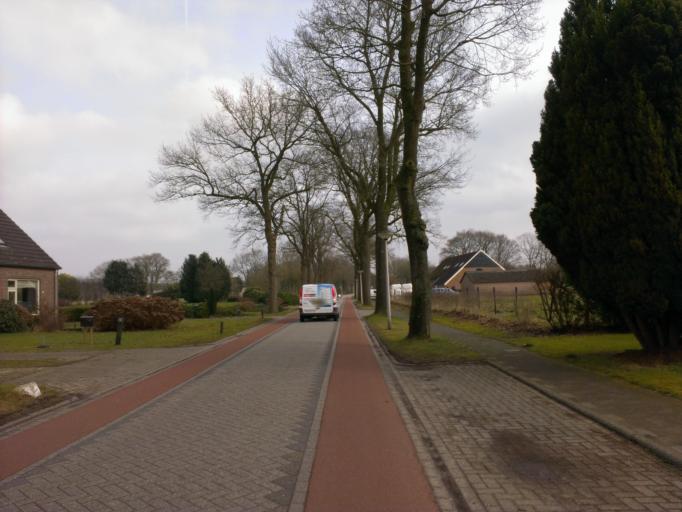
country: NL
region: Drenthe
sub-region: Gemeente Hoogeveen
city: Hoogeveen
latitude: 52.7378
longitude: 6.4577
